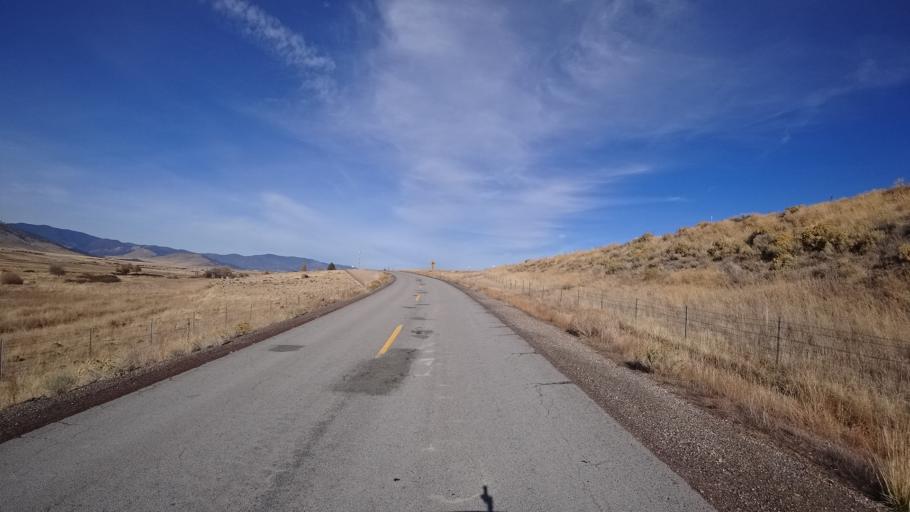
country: US
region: California
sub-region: Siskiyou County
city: Weed
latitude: 41.4735
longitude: -122.4539
